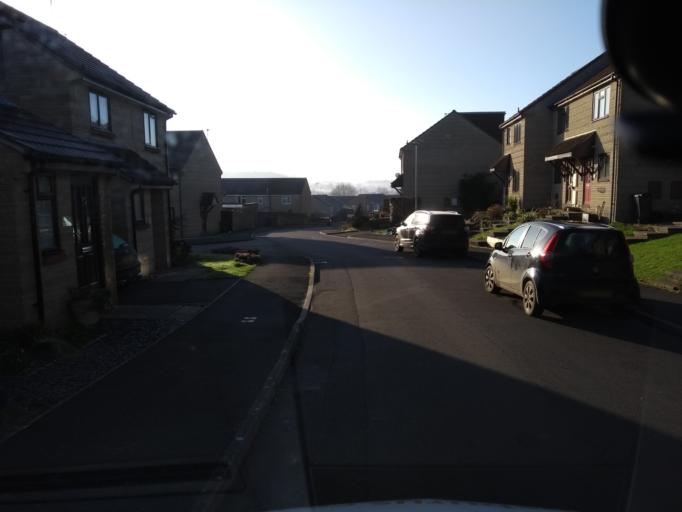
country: GB
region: England
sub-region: Somerset
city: Bruton
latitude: 51.1183
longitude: -2.4482
